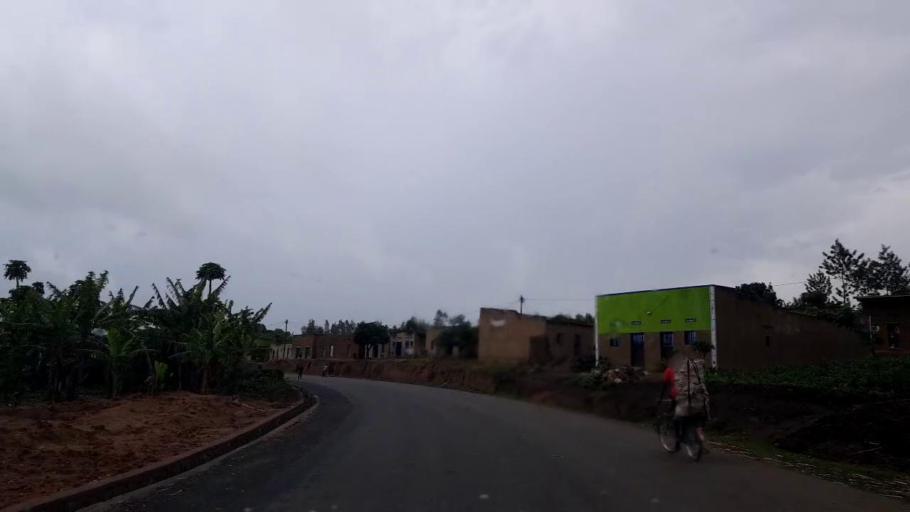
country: RW
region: Northern Province
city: Byumba
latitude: -1.4283
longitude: 30.2756
